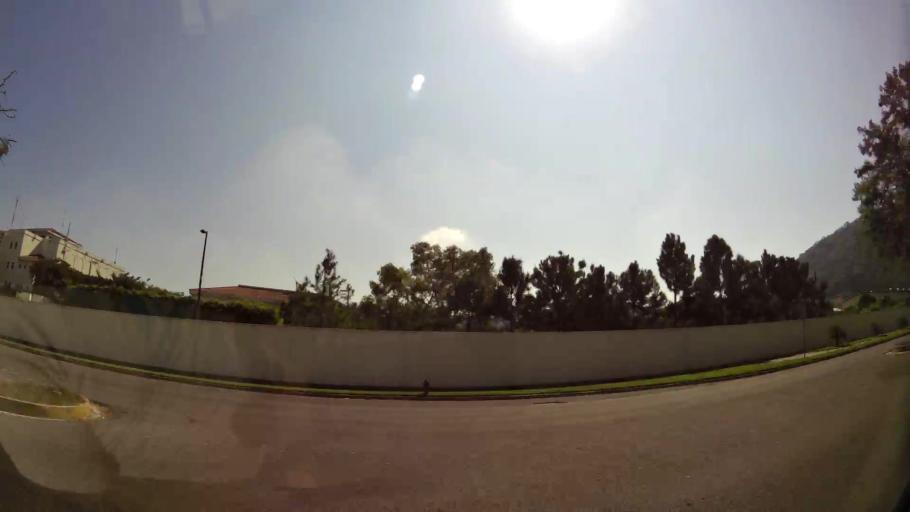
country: SV
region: La Libertad
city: Antiguo Cuscatlan
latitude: 13.6650
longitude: -89.2582
